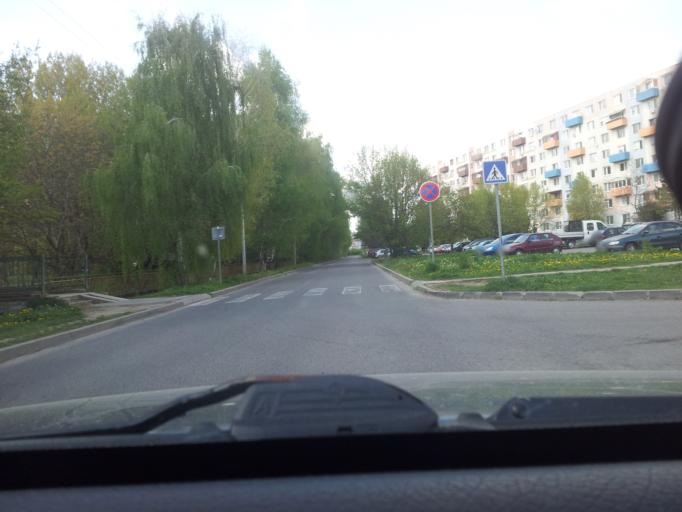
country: SK
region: Nitriansky
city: Levice
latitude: 48.2033
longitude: 18.6083
